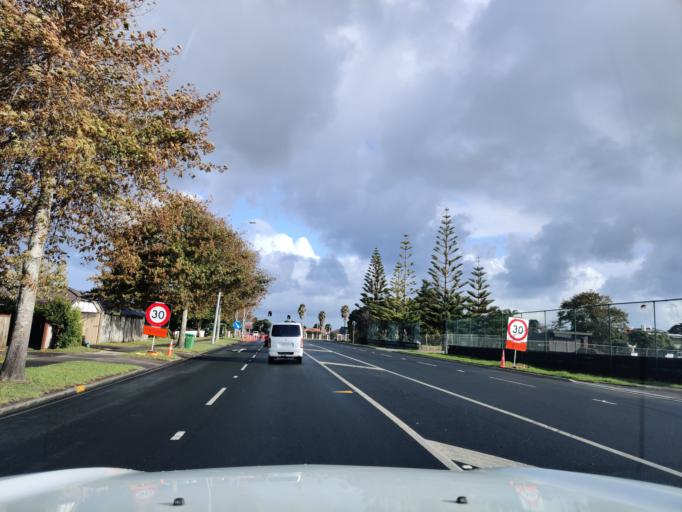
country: NZ
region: Auckland
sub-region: Auckland
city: Pakuranga
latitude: -36.9183
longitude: 174.9133
